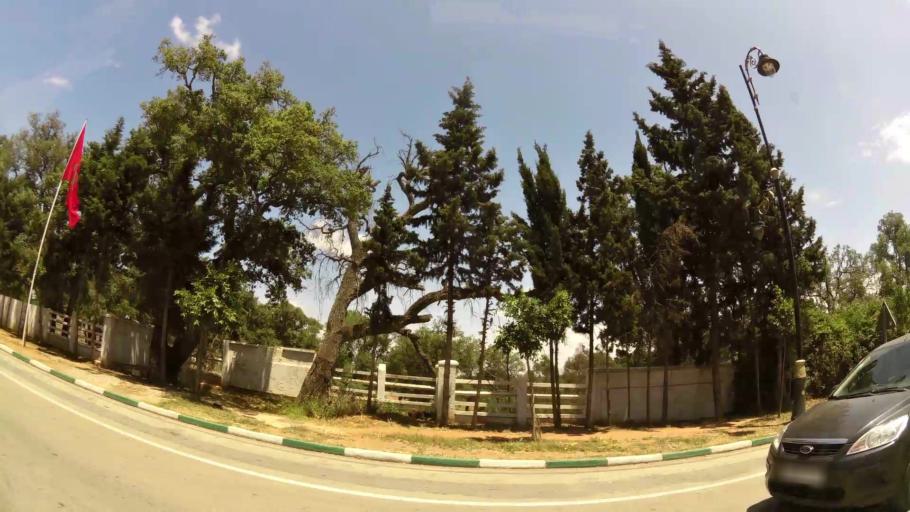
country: MA
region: Gharb-Chrarda-Beni Hssen
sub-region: Kenitra Province
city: Kenitra
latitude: 34.2430
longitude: -6.5726
